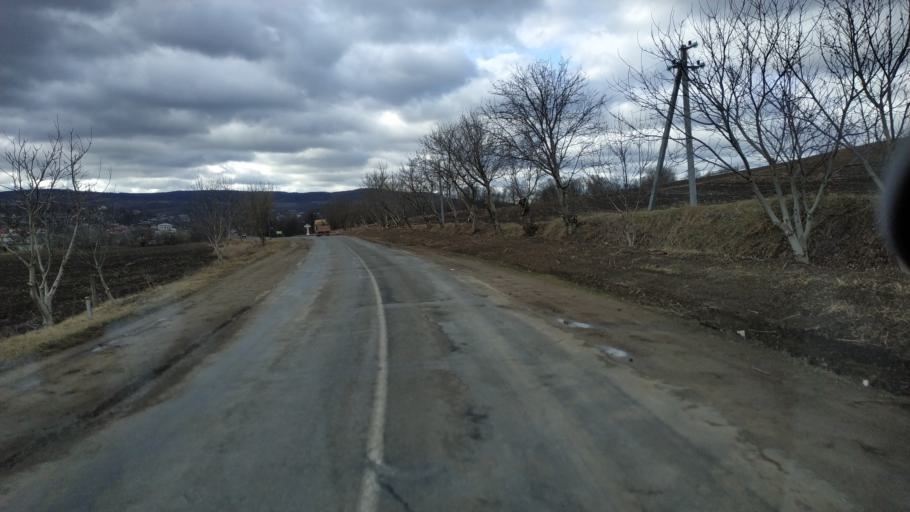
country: MD
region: Stinga Nistrului
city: Bucovat
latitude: 47.1664
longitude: 28.4373
